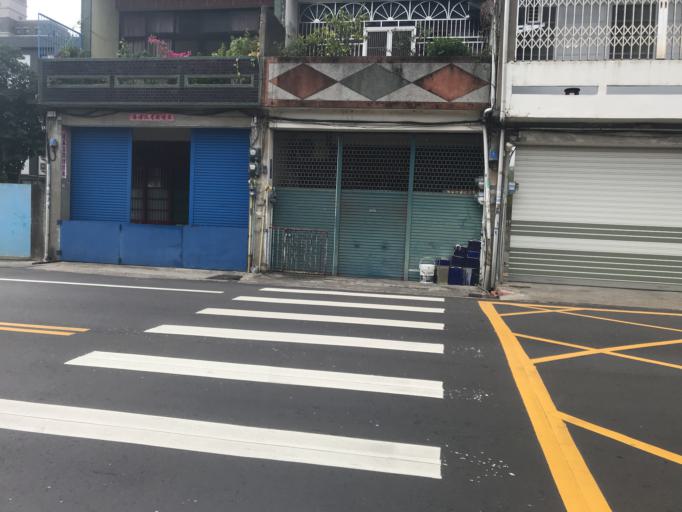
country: TW
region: Taiwan
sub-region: Hsinchu
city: Zhubei
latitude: 24.8209
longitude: 121.0317
